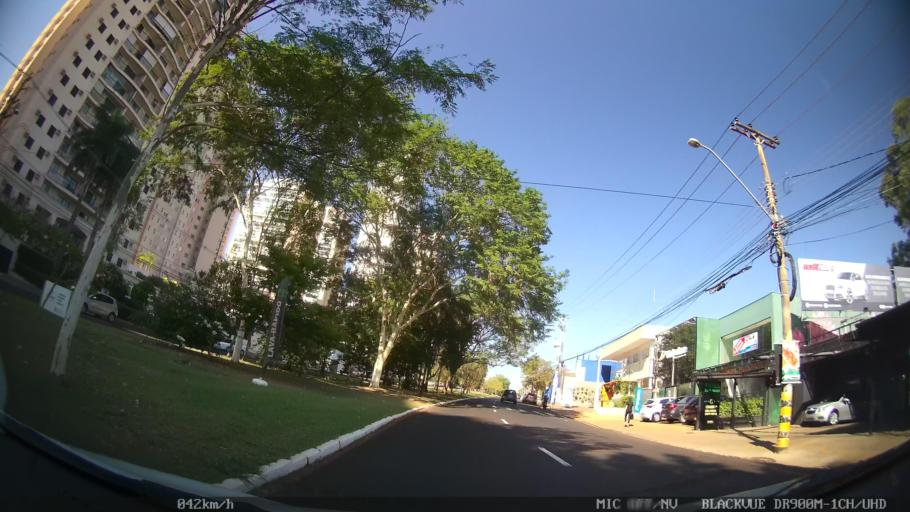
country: BR
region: Sao Paulo
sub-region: Ribeirao Preto
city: Ribeirao Preto
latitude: -21.2139
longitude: -47.8051
